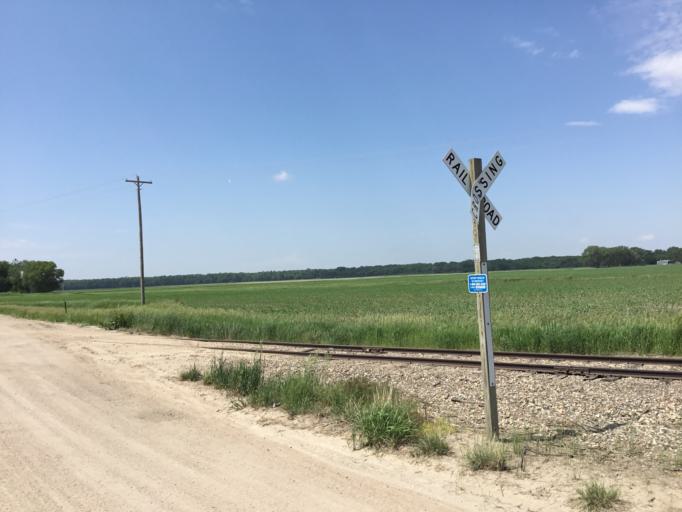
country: US
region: Kansas
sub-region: Republic County
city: Belleville
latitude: 39.7578
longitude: -97.7819
